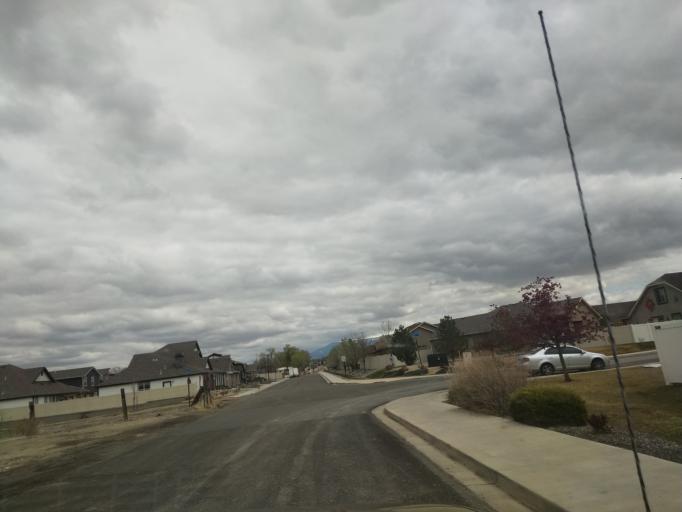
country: US
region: Colorado
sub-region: Mesa County
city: Redlands
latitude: 39.1027
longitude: -108.5945
